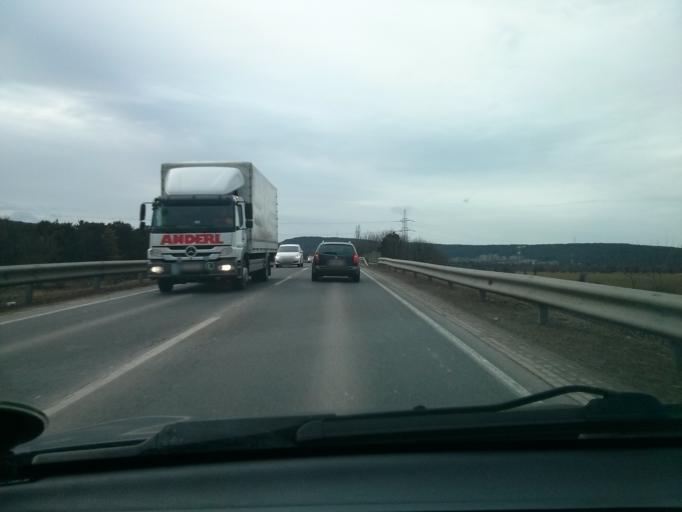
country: AT
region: Lower Austria
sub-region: Politischer Bezirk Wiener Neustadt
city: Theresienfeld
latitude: 47.8524
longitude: 16.1915
